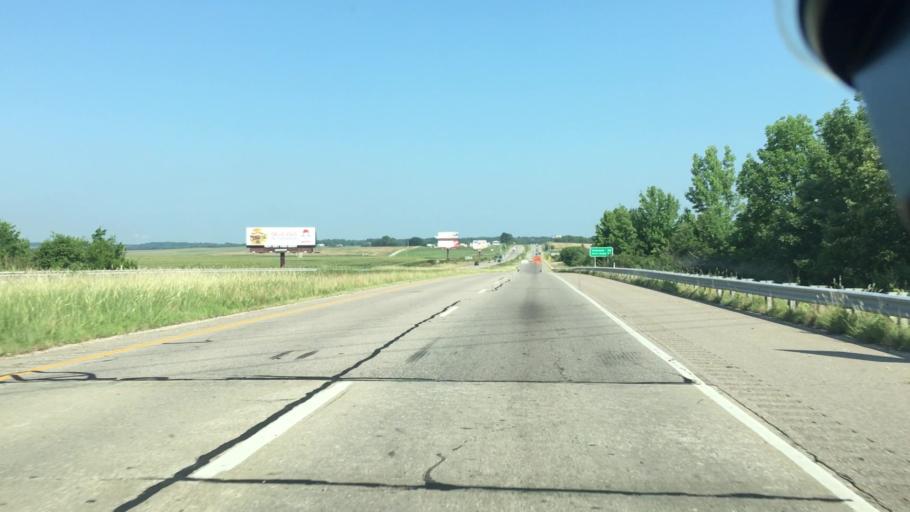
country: US
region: Indiana
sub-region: Gibson County
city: Princeton
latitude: 38.3206
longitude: -87.5761
